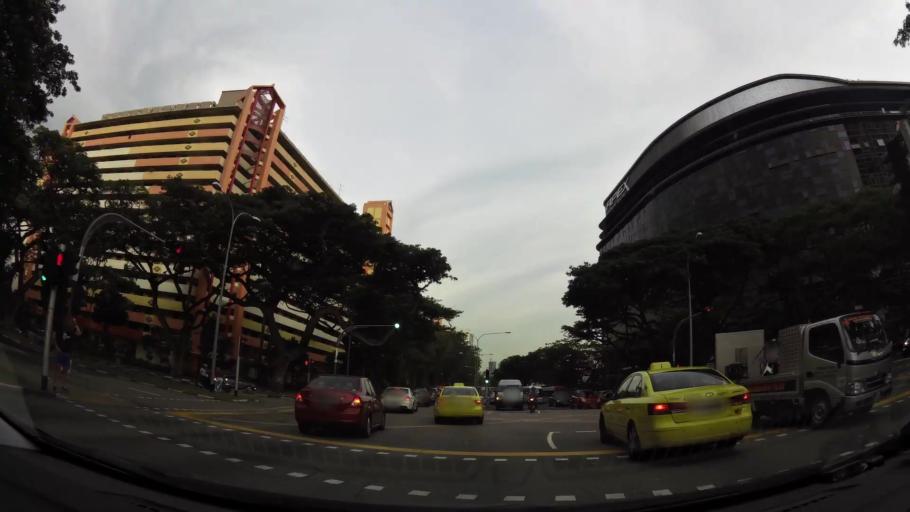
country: SG
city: Singapore
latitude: 1.2834
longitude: 103.8201
